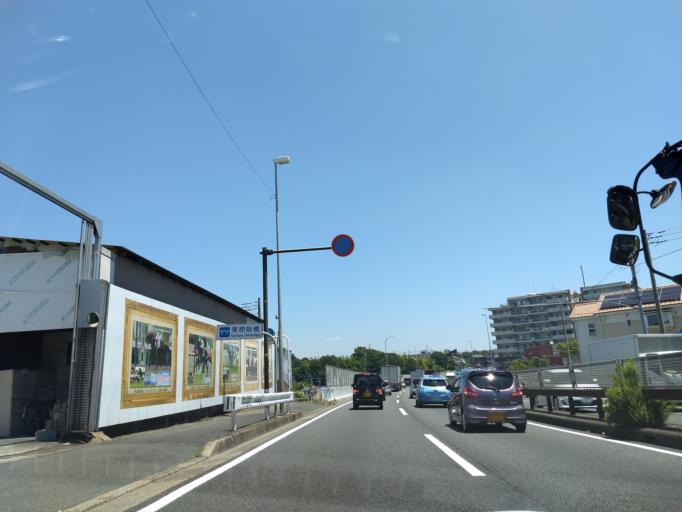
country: JP
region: Kanagawa
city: Zama
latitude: 35.4779
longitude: 139.4175
